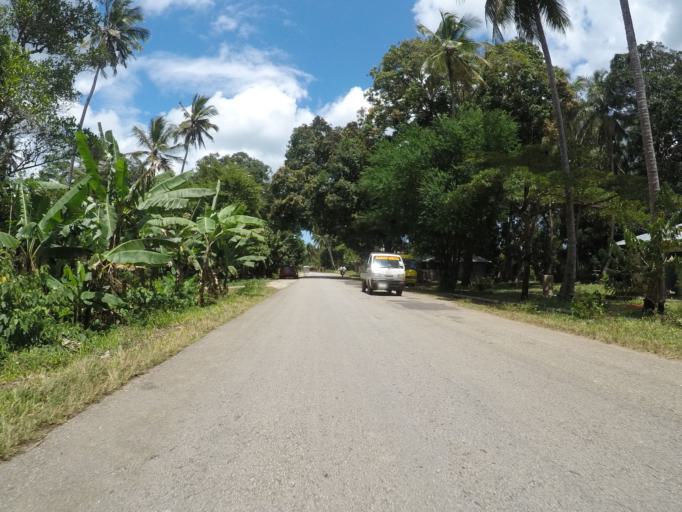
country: TZ
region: Zanzibar Central/South
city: Mahonda
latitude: -6.3009
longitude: 39.4331
